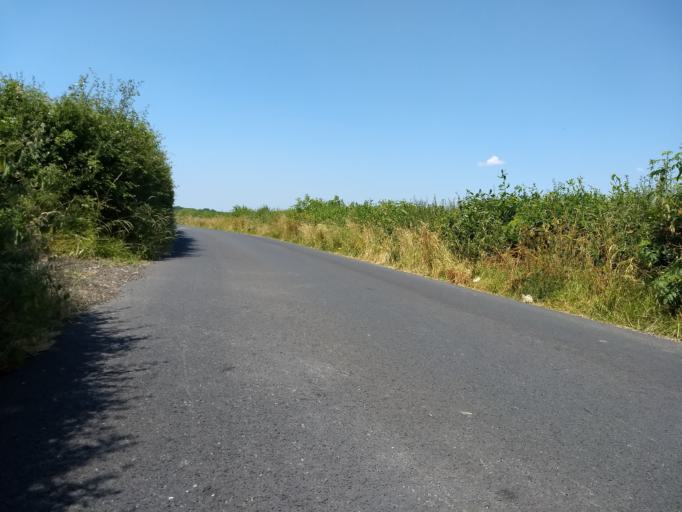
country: GB
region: England
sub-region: Isle of Wight
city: Northwood
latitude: 50.7098
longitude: -1.3577
